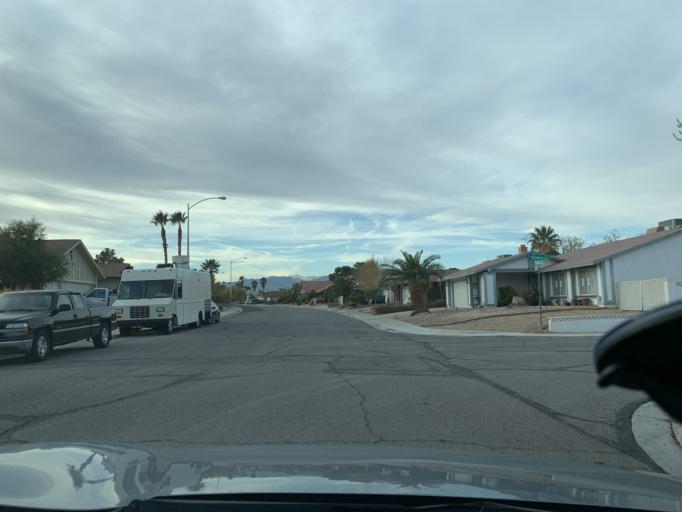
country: US
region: Nevada
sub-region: Clark County
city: Spring Valley
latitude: 36.0960
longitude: -115.2291
